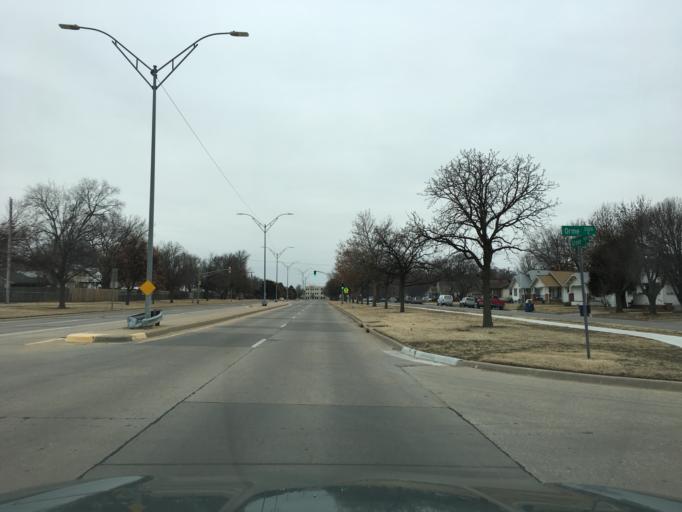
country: US
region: Kansas
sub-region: Sedgwick County
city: Wichita
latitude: 37.6774
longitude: -97.3083
